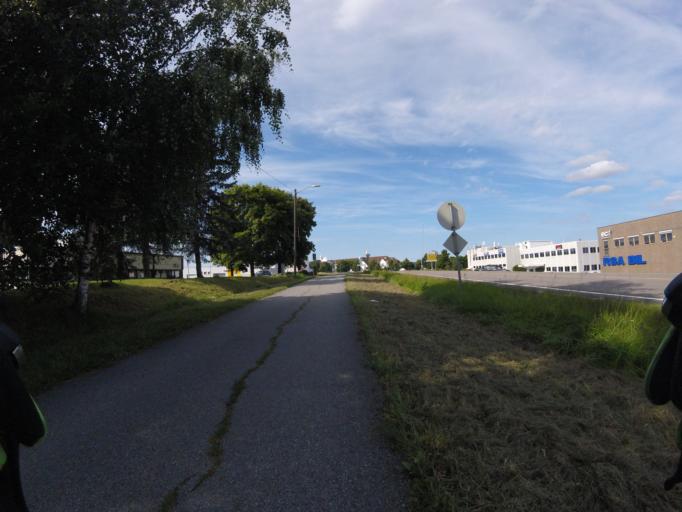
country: NO
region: Akershus
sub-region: Skedsmo
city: Lillestrom
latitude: 59.9771
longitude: 11.0016
